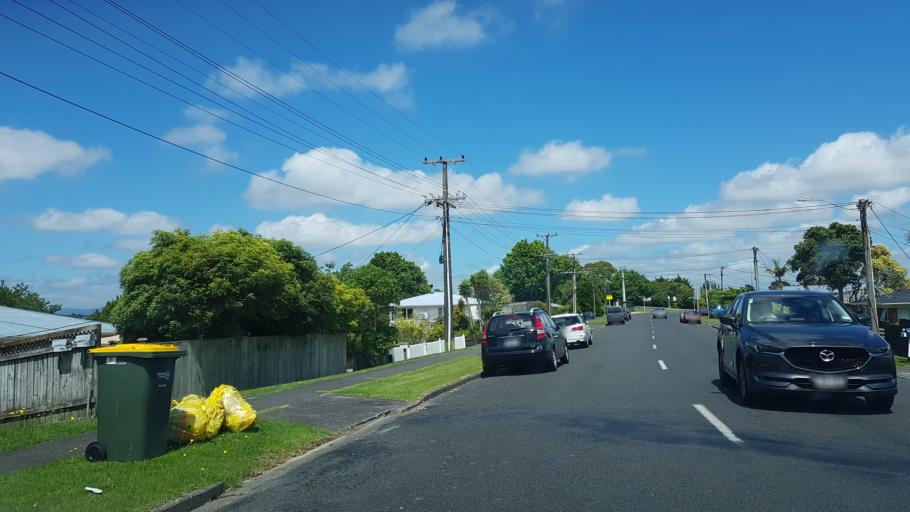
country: NZ
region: Auckland
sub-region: Auckland
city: North Shore
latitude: -36.7897
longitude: 174.7157
